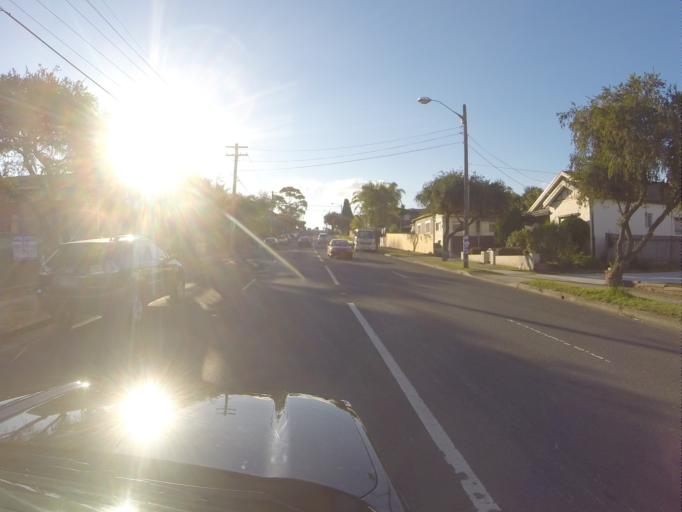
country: AU
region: New South Wales
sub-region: Canterbury
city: Canterbury
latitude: -33.9222
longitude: 151.1069
